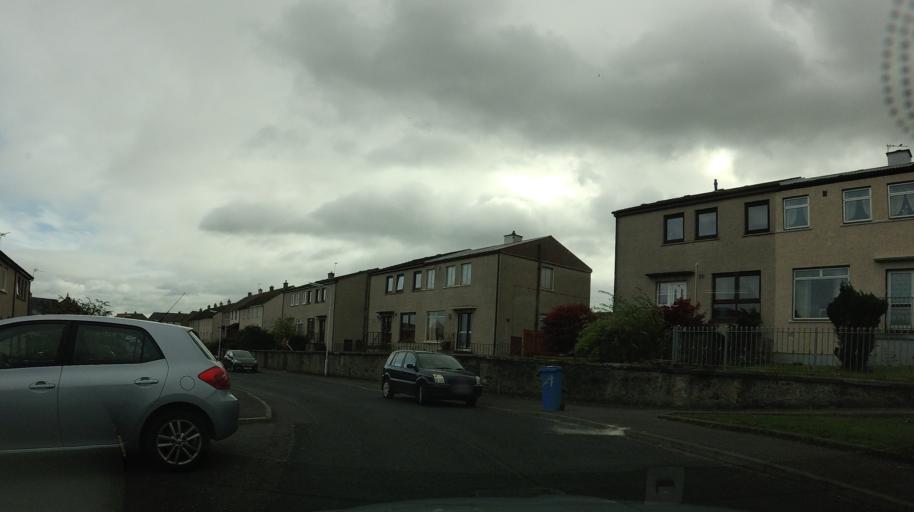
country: GB
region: Scotland
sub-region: Fife
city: Cowdenbeath
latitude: 56.0997
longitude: -3.3619
